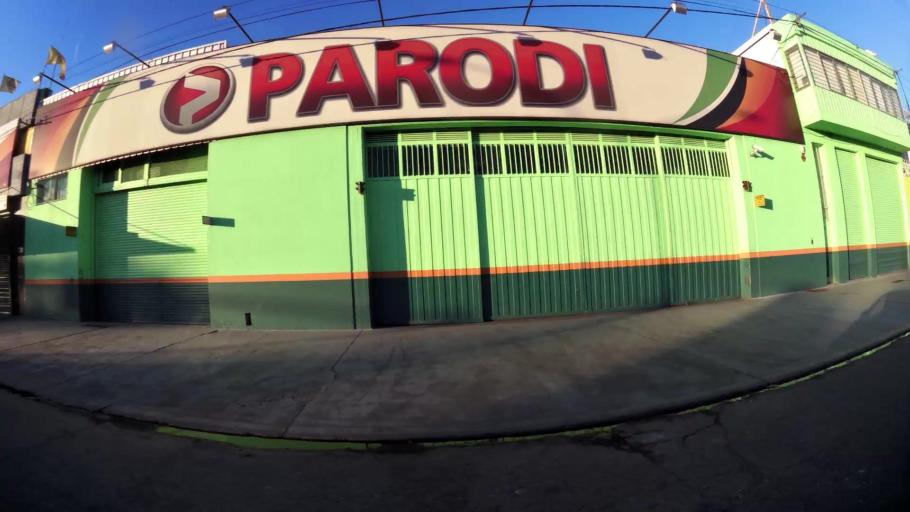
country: AR
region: Santa Fe
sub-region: Departamento de Rosario
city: Rosario
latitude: -32.9611
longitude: -60.6797
